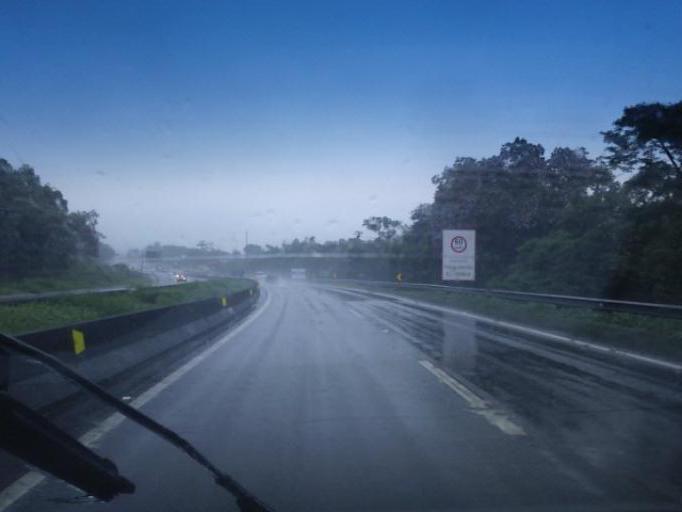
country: BR
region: Parana
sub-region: Guaratuba
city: Guaratuba
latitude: -25.9745
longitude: -48.8897
